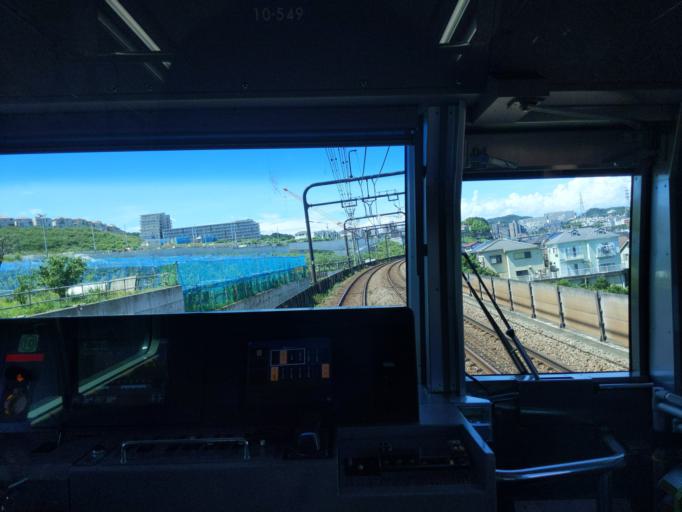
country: JP
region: Tokyo
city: Chofugaoka
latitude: 35.6331
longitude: 139.5110
